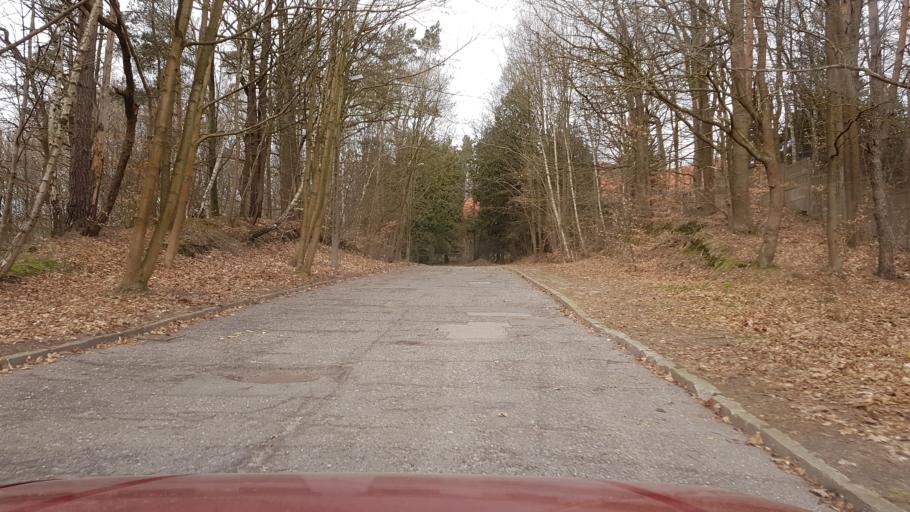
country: PL
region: West Pomeranian Voivodeship
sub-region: Koszalin
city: Koszalin
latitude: 54.1970
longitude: 16.2301
